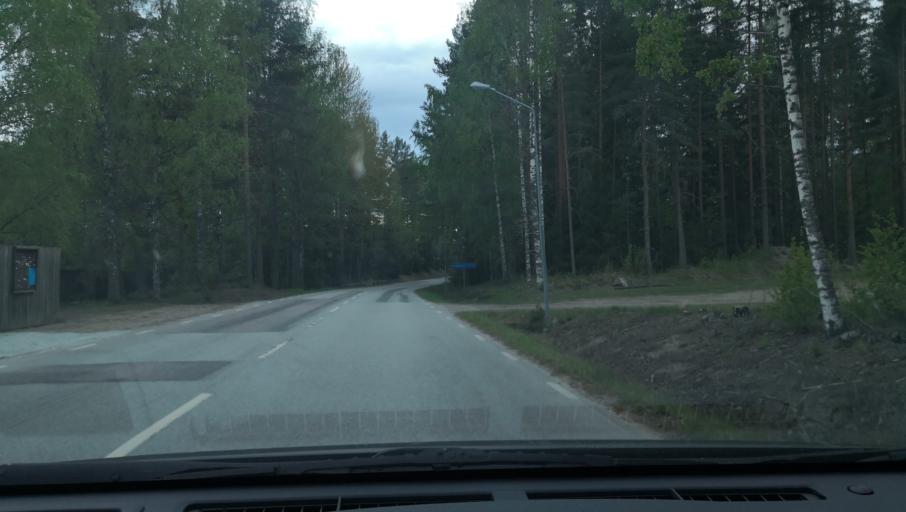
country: SE
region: Vaestmanland
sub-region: Skinnskattebergs Kommun
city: Skinnskatteberg
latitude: 59.8099
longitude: 15.5558
